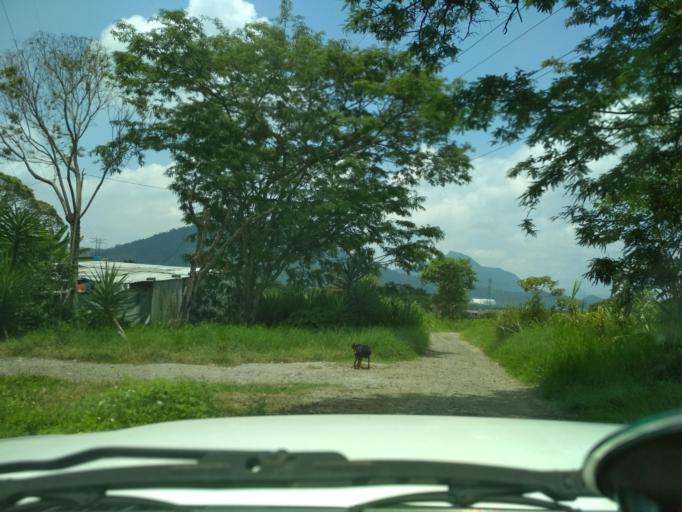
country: MX
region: Veracruz
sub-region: Ixtaczoquitlan
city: Buenavista
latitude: 18.8859
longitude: -97.0633
